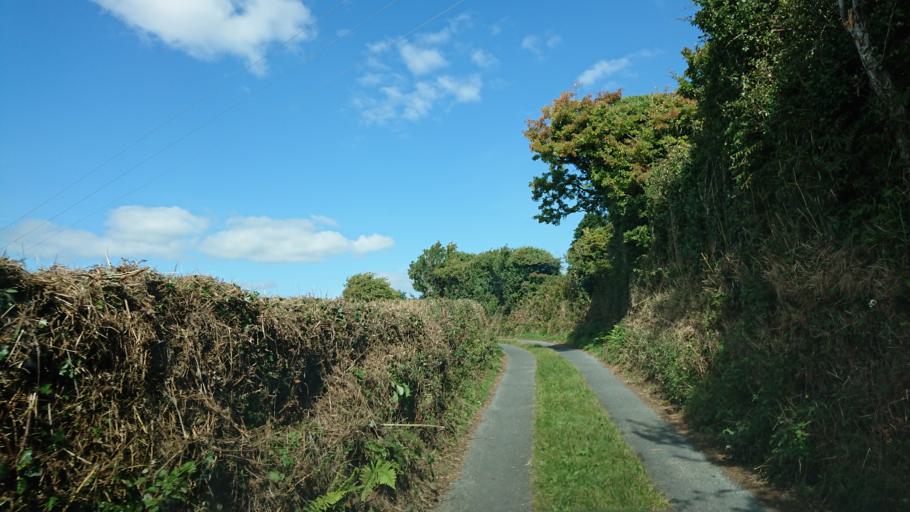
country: IE
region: Munster
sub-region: Waterford
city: Waterford
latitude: 52.2317
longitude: -7.1560
